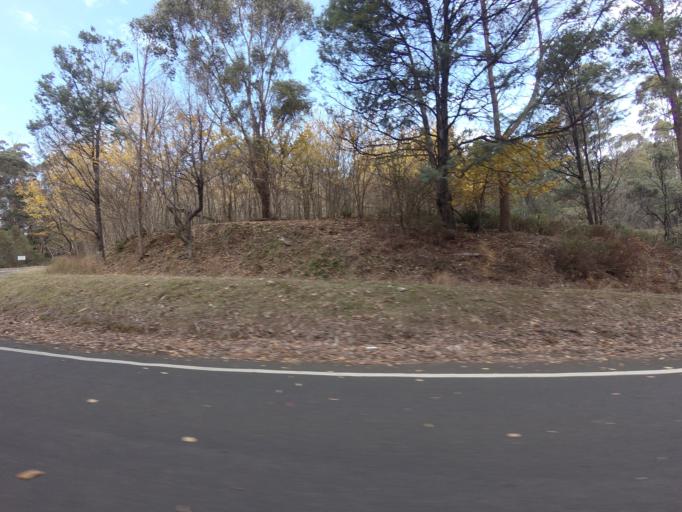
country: AU
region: Tasmania
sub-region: Meander Valley
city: Deloraine
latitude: -41.6393
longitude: 146.7160
